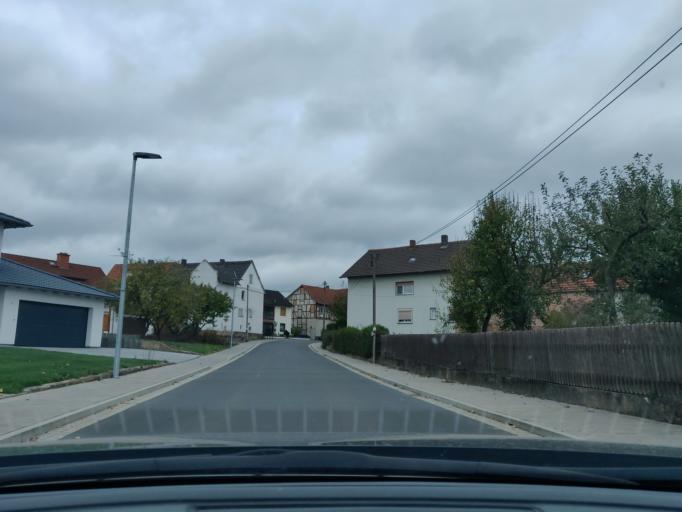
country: DE
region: Hesse
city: Fritzlar
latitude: 51.1809
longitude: 9.2704
